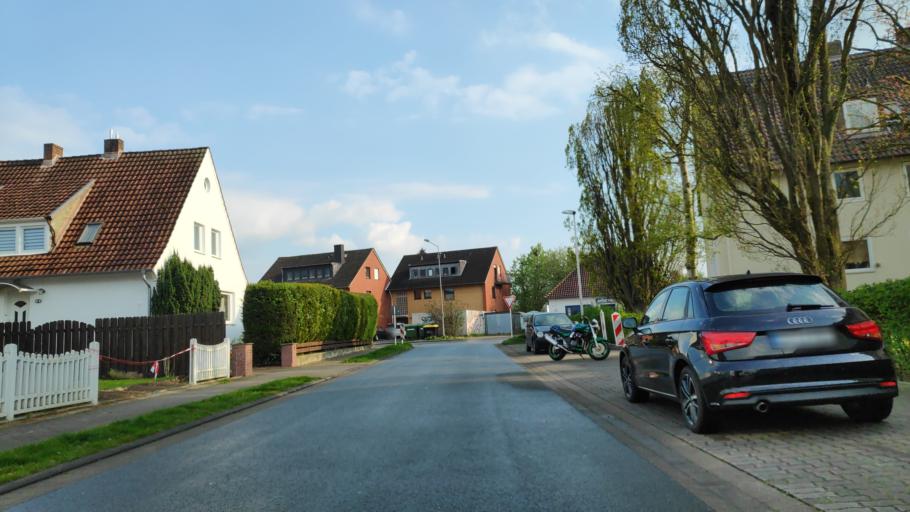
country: DE
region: North Rhine-Westphalia
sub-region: Regierungsbezirk Detmold
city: Minden
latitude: 52.2890
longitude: 8.9492
